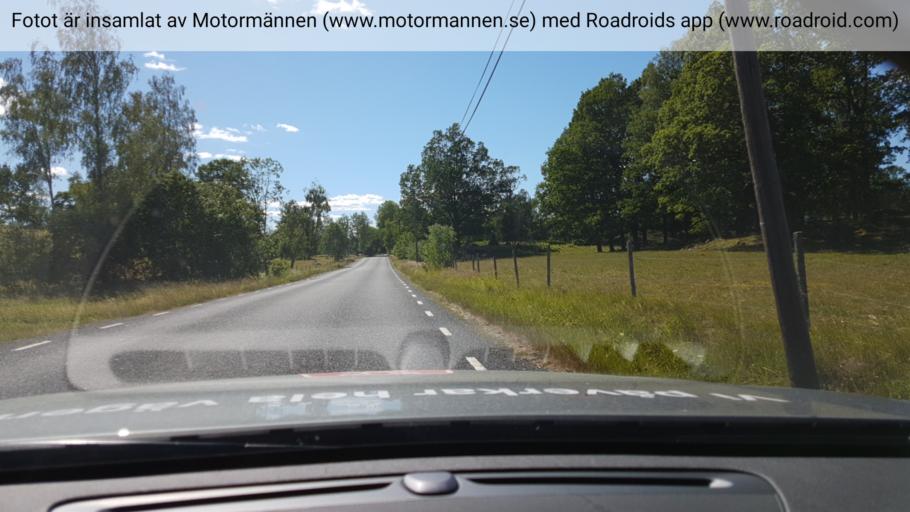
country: SE
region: Soedermanland
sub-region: Flens Kommun
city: Halleforsnas
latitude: 59.1628
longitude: 16.5191
